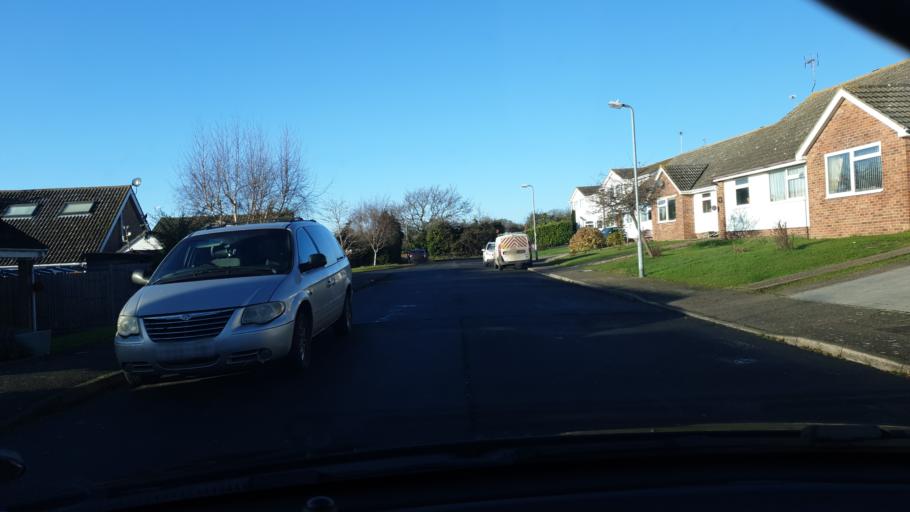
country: GB
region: England
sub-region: Essex
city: Brightlingsea
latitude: 51.8151
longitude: 1.0171
